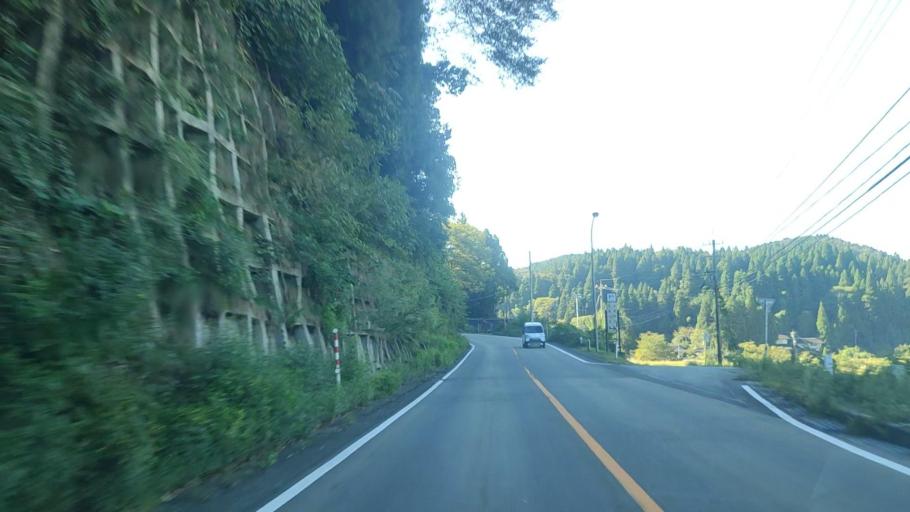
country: JP
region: Ishikawa
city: Nanao
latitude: 37.2828
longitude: 137.0353
